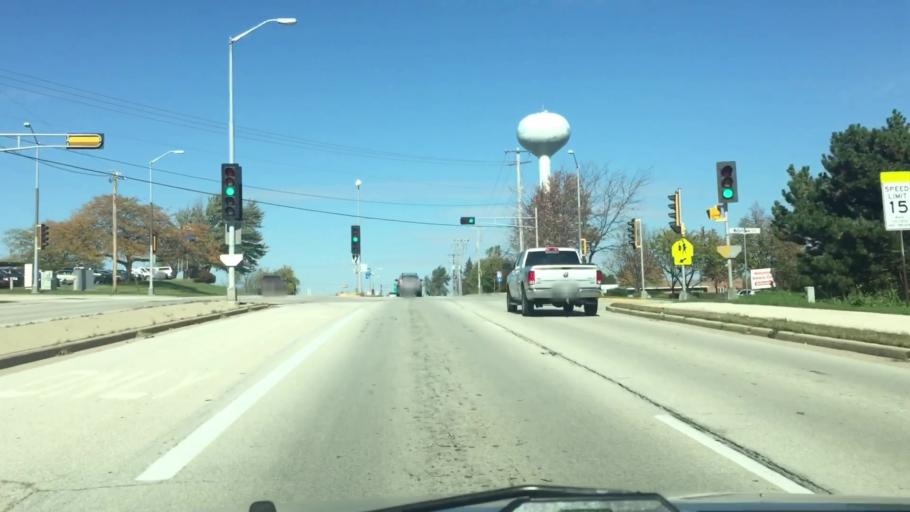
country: US
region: Wisconsin
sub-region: Waukesha County
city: Waukesha
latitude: 43.0300
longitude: -88.1668
